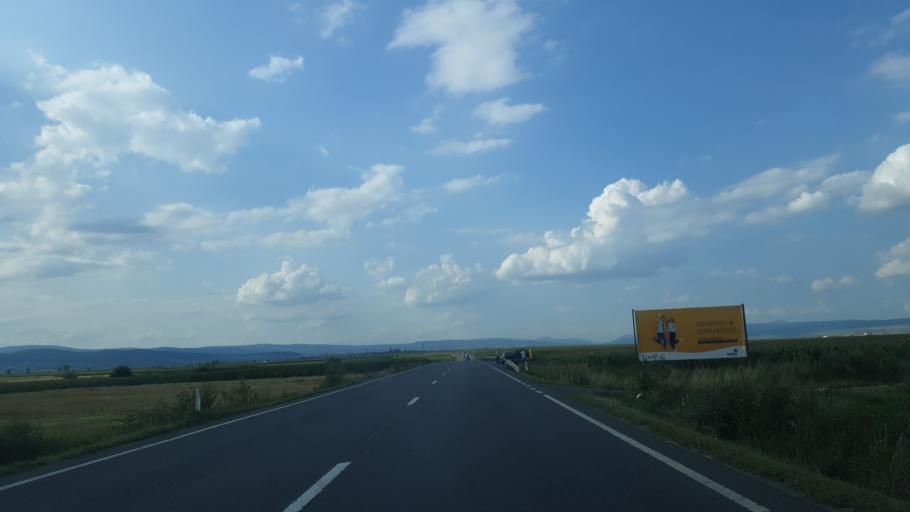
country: RO
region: Covasna
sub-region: Comuna Chichis
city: Chichis
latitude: 45.7865
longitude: 25.8071
